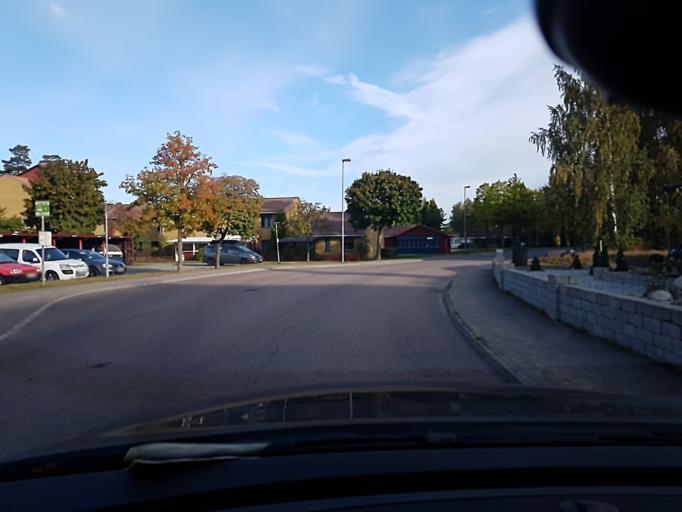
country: SE
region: Kronoberg
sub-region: Vaxjo Kommun
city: Vaexjoe
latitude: 56.8460
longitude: 14.8159
